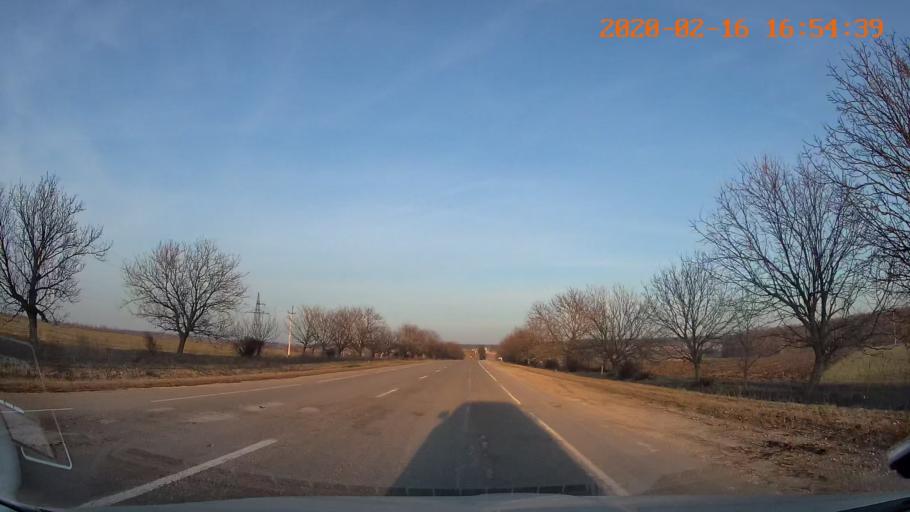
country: MD
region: Briceni
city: Briceni
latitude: 48.3228
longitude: 27.0115
